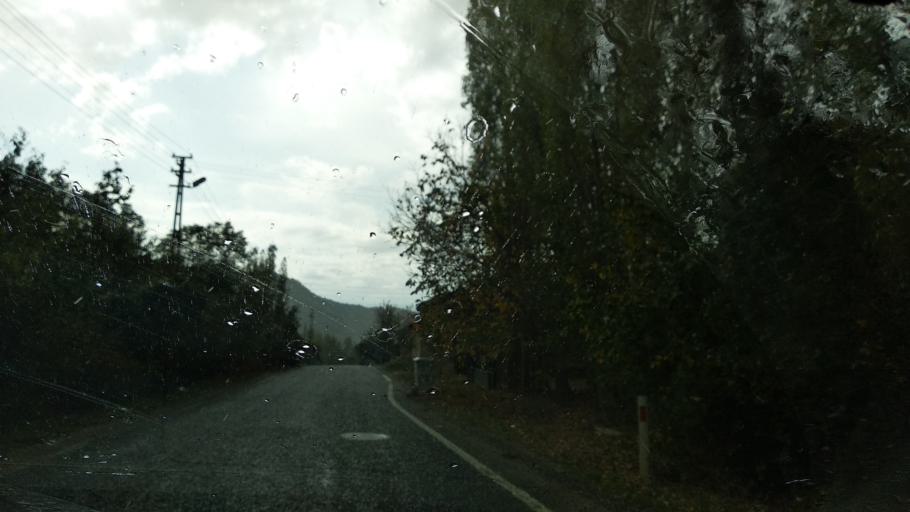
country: TR
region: Ankara
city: Nallihan
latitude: 40.3313
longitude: 31.4122
